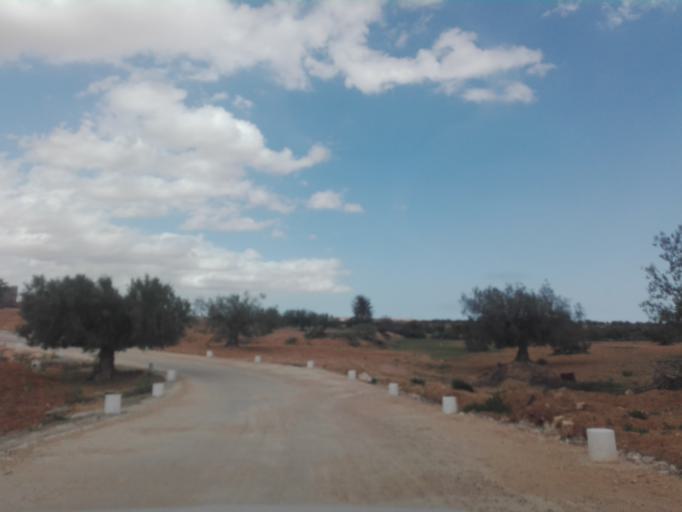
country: TN
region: Safaqis
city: Sfax
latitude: 34.6884
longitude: 10.4483
